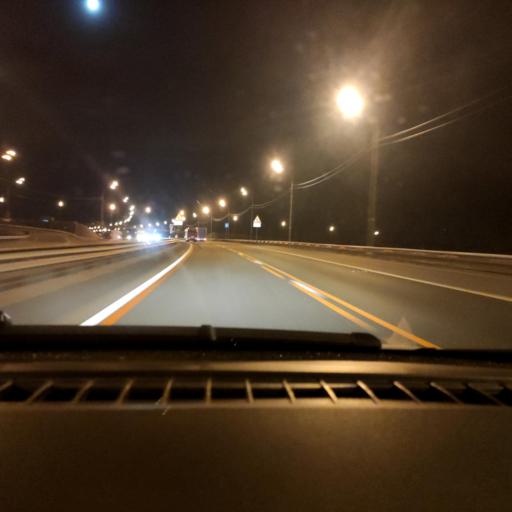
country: RU
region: Lipetsk
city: Khlevnoye
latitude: 52.2405
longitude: 39.0696
